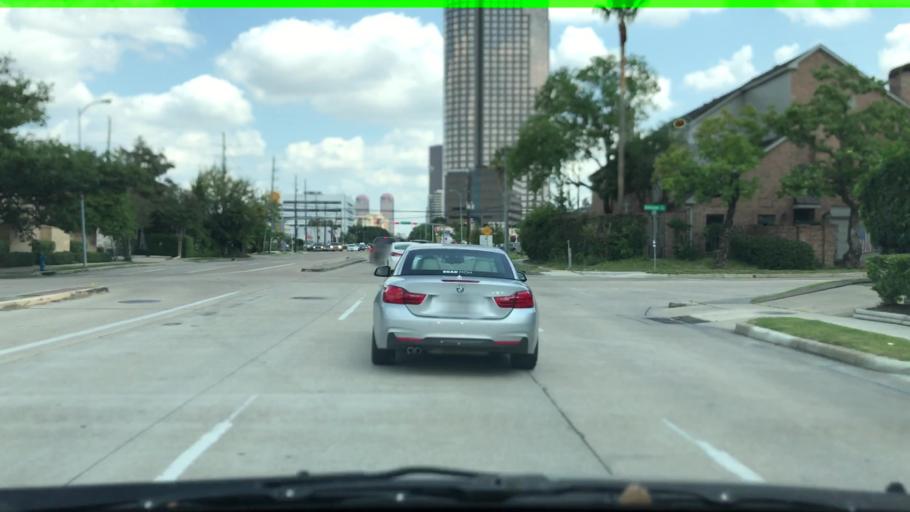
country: US
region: Texas
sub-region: Harris County
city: Hunters Creek Village
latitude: 29.7498
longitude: -95.4877
